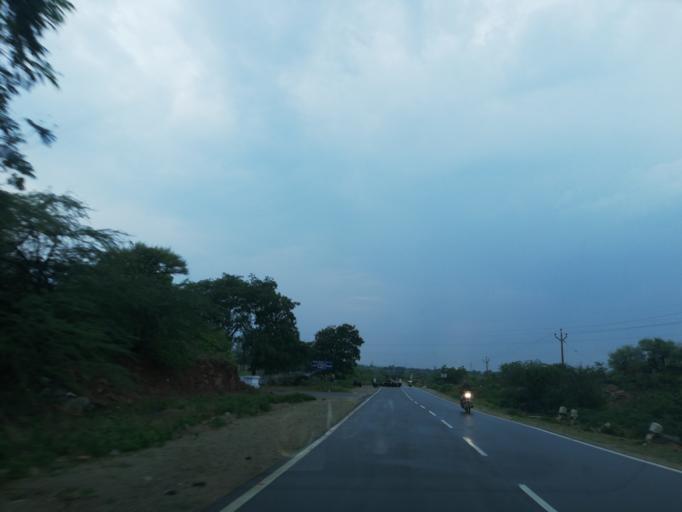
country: IN
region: Andhra Pradesh
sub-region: Guntur
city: Macherla
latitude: 16.6653
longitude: 79.2847
